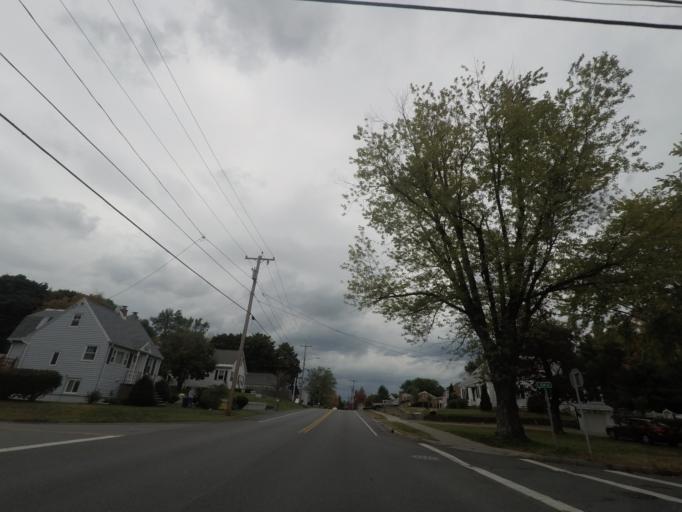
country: US
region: New York
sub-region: Albany County
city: McKownville
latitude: 42.6676
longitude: -73.8473
